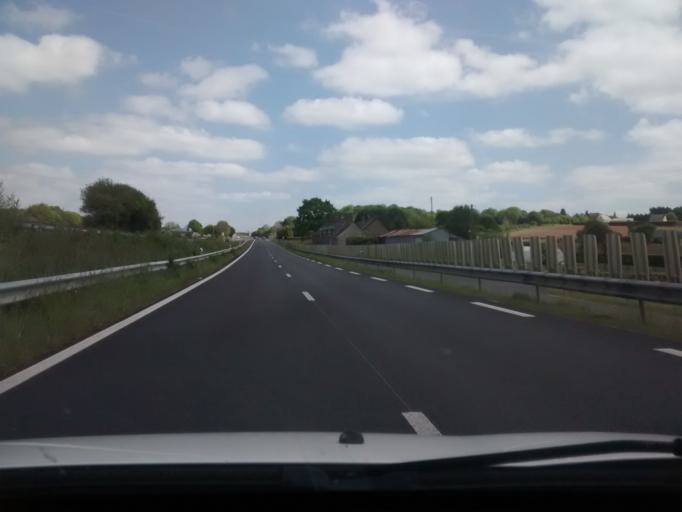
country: FR
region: Brittany
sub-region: Departement des Cotes-d'Armor
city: Pedernec
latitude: 48.5838
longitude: -3.2447
